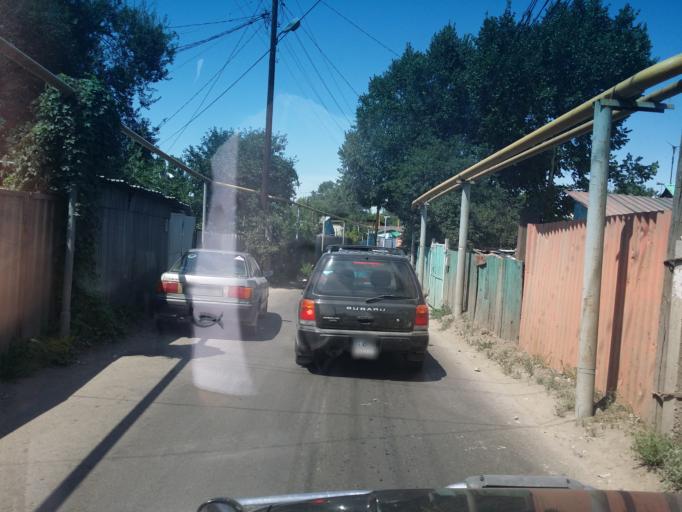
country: KZ
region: Almaty Qalasy
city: Almaty
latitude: 43.2645
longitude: 76.9129
